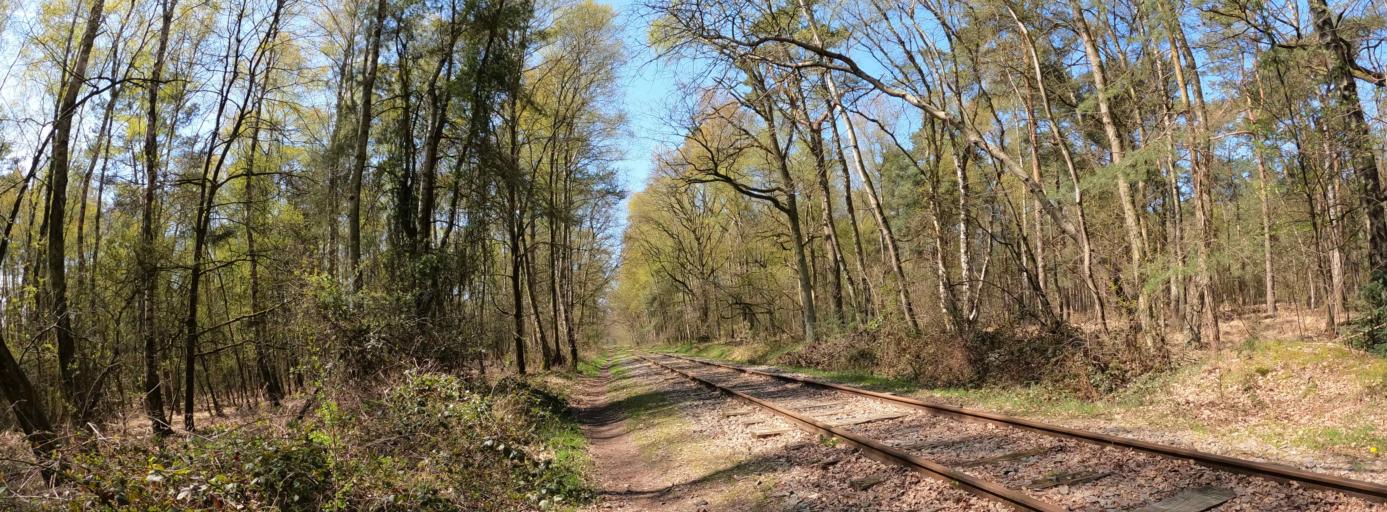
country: BE
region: Flanders
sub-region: Provincie Antwerpen
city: Brasschaat
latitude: 51.3351
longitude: 4.4901
